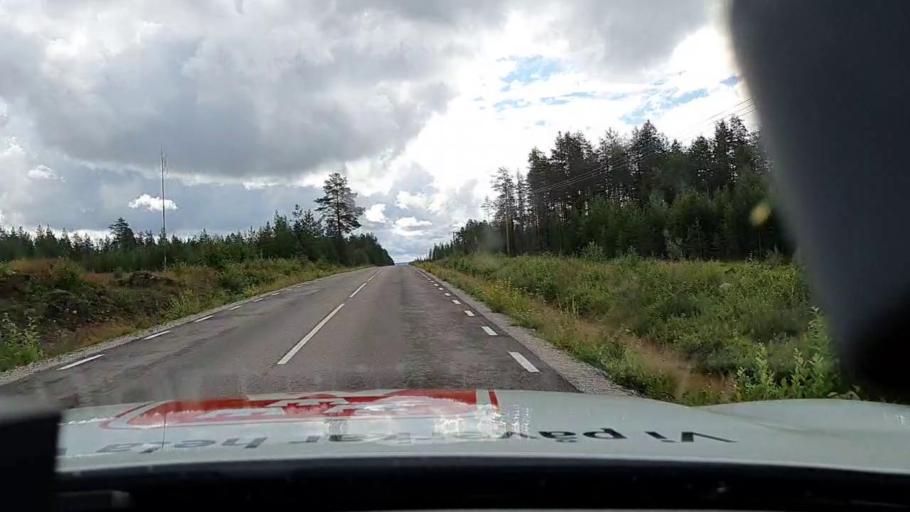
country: SE
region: Norrbotten
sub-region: Overkalix Kommun
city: OEverkalix
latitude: 66.2574
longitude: 22.8582
